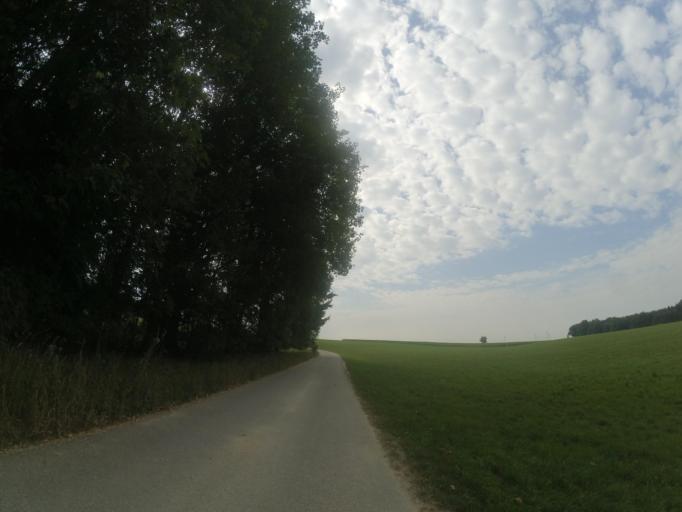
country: DE
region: Baden-Wuerttemberg
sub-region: Tuebingen Region
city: Lonsee
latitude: 48.5006
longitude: 9.8933
